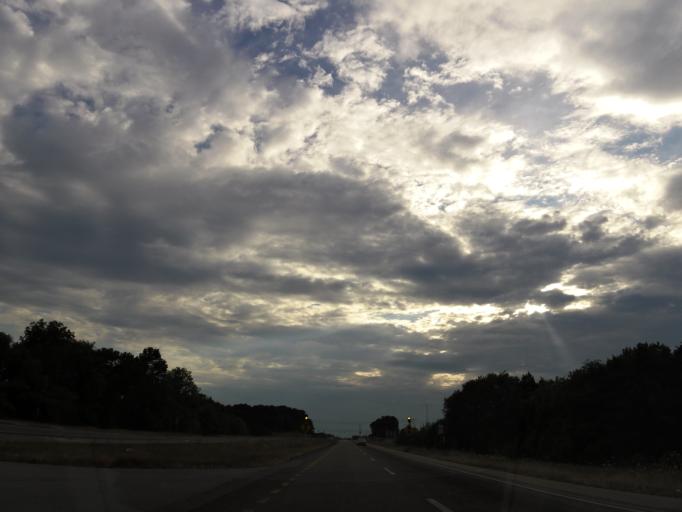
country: US
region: Alabama
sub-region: Lawrence County
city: Moulton
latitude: 34.4919
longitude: -87.2876
